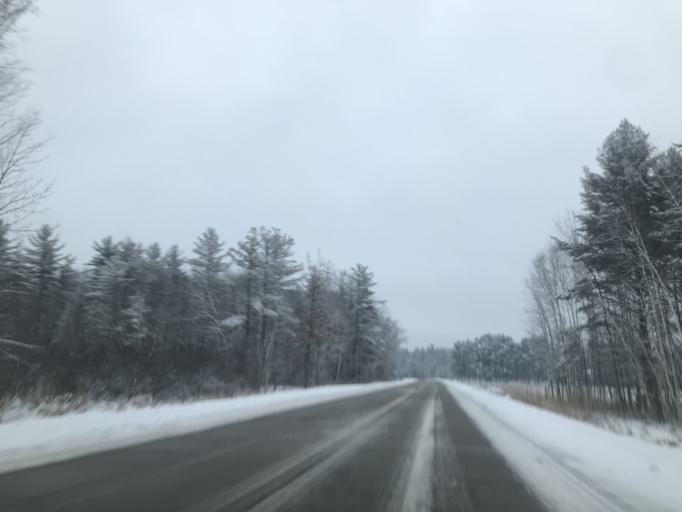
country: US
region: Wisconsin
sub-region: Oconto County
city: Oconto Falls
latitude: 44.8624
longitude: -88.1152
